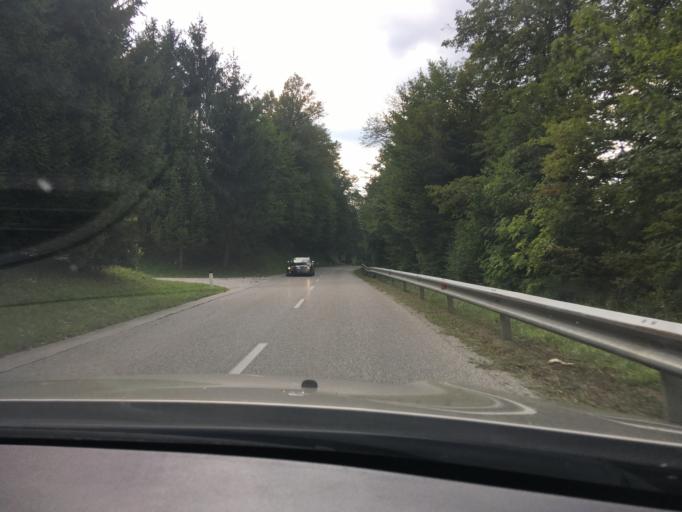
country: SI
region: Straza
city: Straza
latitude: 45.7737
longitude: 15.0583
